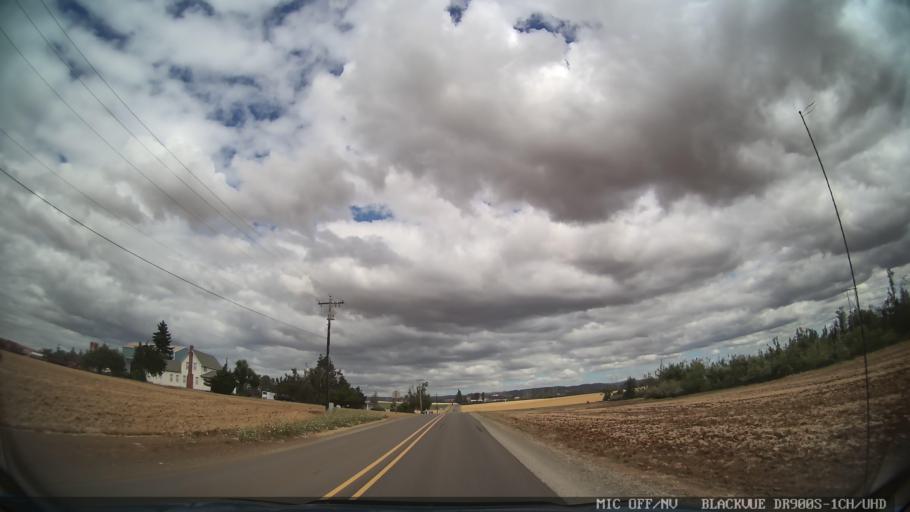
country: US
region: Oregon
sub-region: Marion County
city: Sublimity
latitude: 44.8662
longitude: -122.7882
